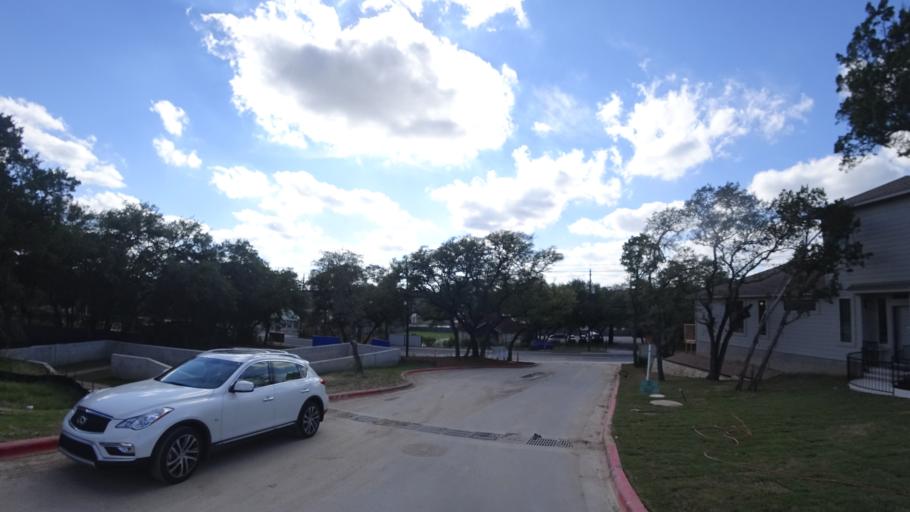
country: US
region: Texas
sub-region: Travis County
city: Barton Creek
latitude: 30.2413
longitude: -97.8769
